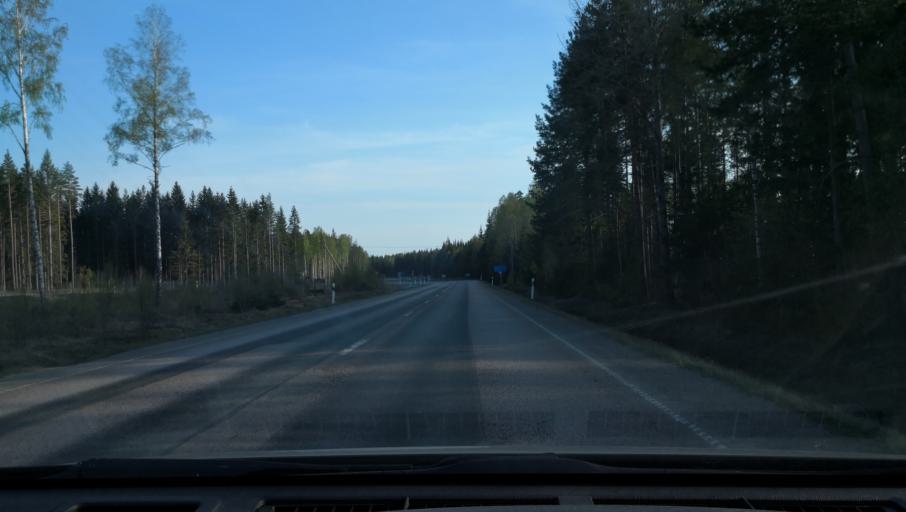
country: SE
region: Uppsala
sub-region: Heby Kommun
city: Heby
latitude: 59.9705
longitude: 16.8356
